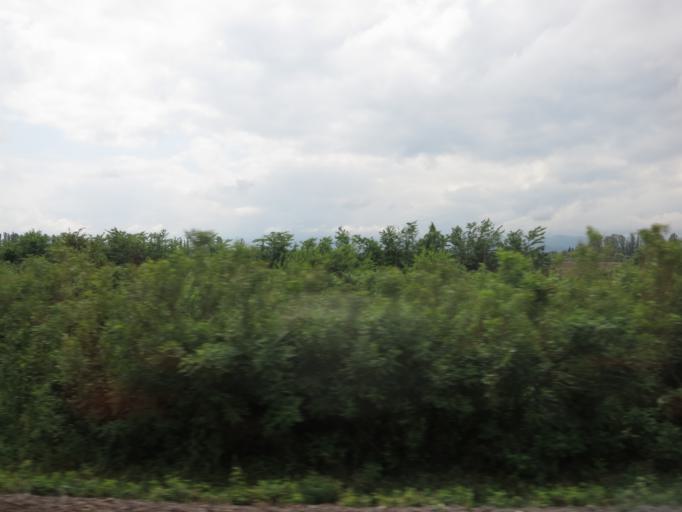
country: GE
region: Imereti
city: K'ulashi
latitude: 42.1825
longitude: 42.4395
